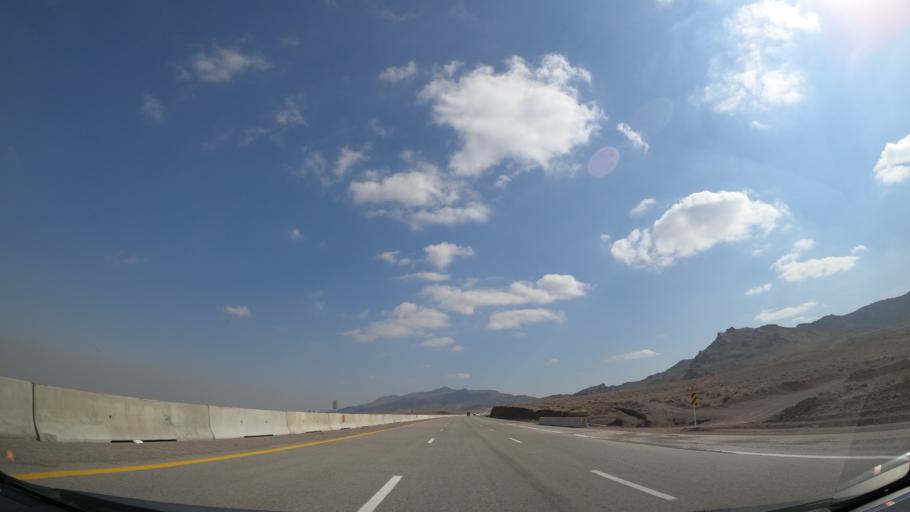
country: IR
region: Alborz
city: Eshtehard
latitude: 35.7063
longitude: 50.6088
